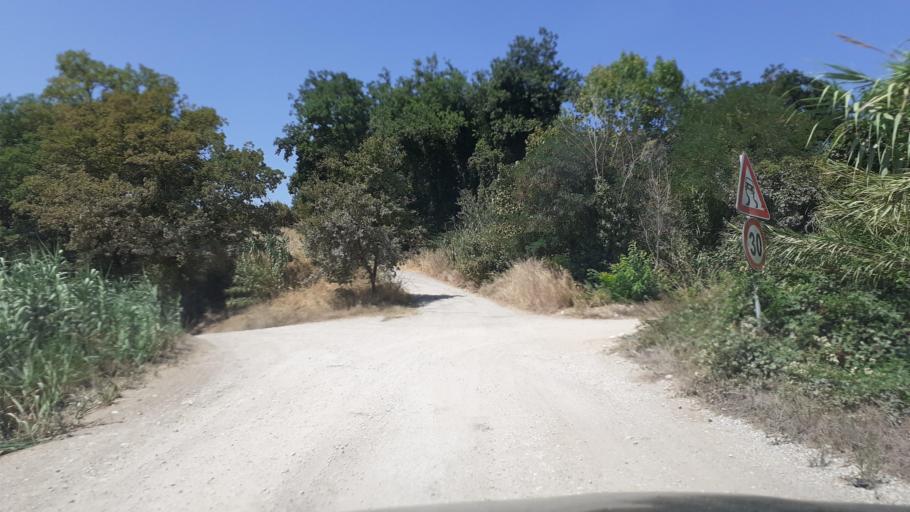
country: IT
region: Abruzzo
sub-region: Provincia di Chieti
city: Santa Maria Imbaro
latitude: 42.2067
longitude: 14.4825
